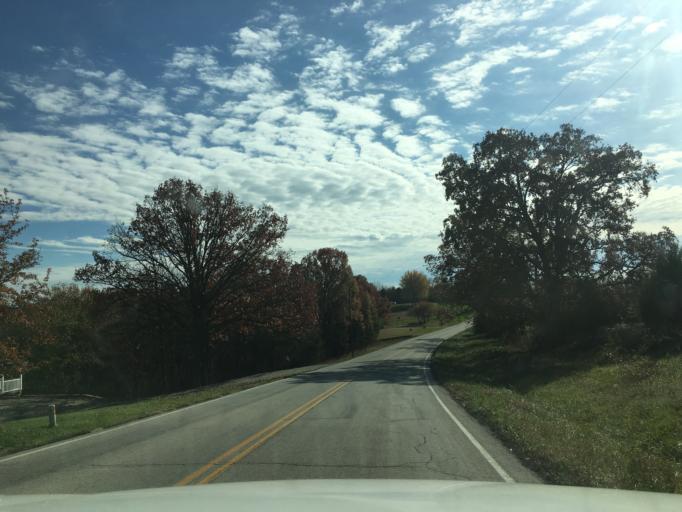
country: US
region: Missouri
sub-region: Osage County
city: Linn
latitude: 38.4253
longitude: -91.8248
